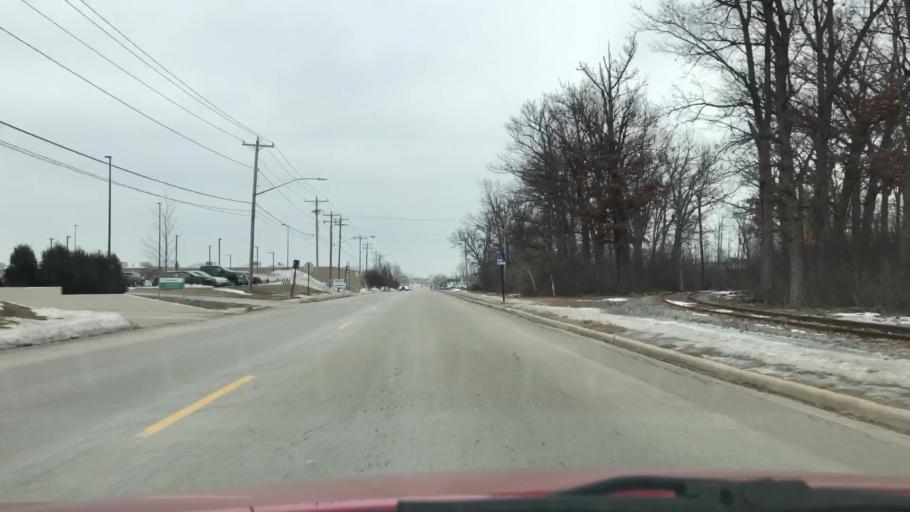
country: US
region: Wisconsin
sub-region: Brown County
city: Ashwaubenon
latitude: 44.4707
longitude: -88.0725
